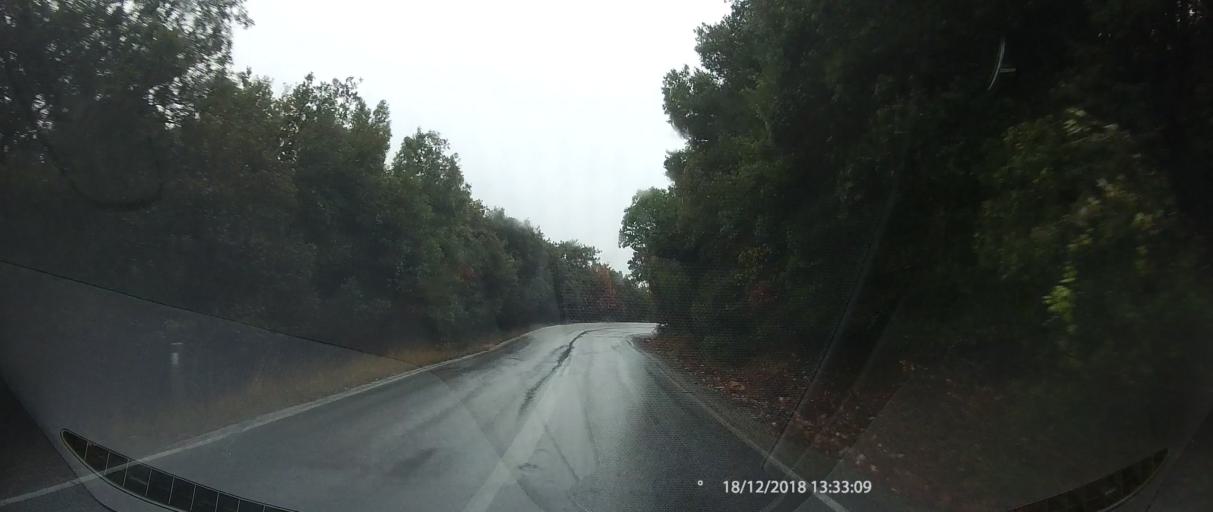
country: GR
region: Central Macedonia
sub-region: Nomos Pierias
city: Litochoro
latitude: 40.1183
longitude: 22.4786
